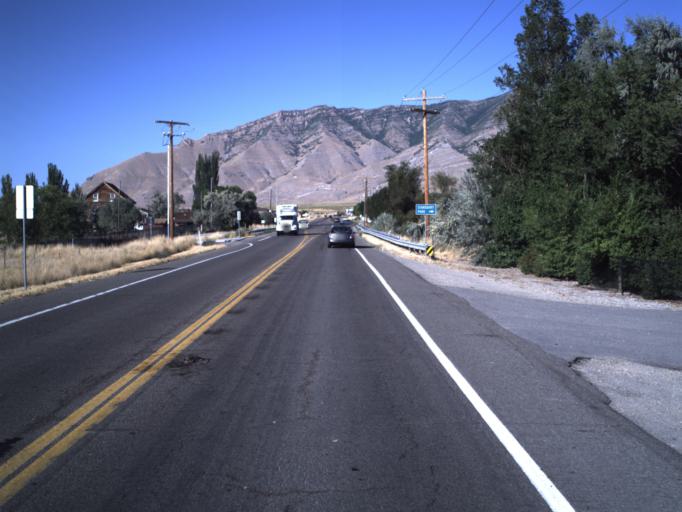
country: US
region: Utah
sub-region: Tooele County
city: Stansbury park
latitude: 40.6494
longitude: -112.2986
